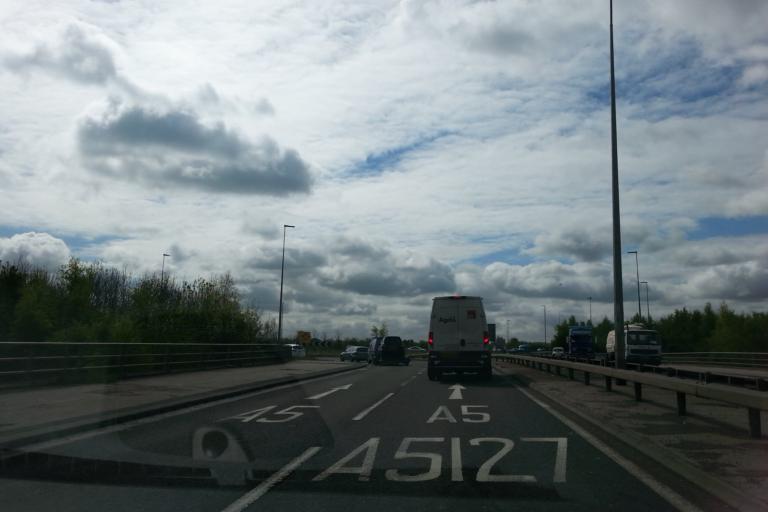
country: GB
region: England
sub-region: Staffordshire
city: Shenstone
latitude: 52.6505
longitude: -1.8340
